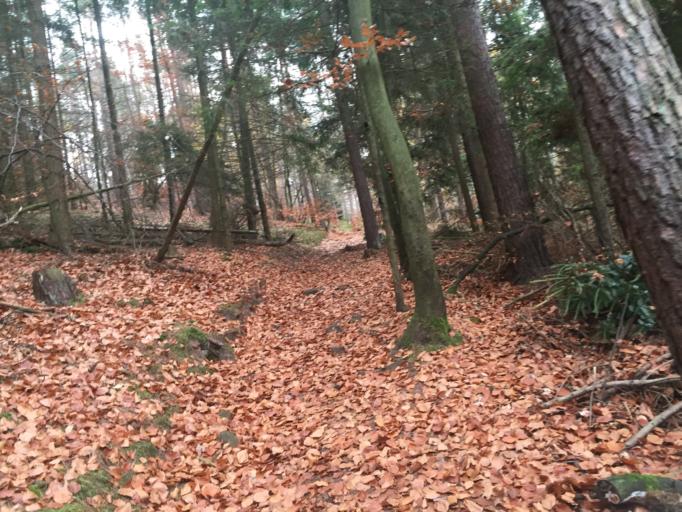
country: DE
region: Rheinland-Pfalz
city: Carlsberg
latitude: 49.4882
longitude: 8.0217
